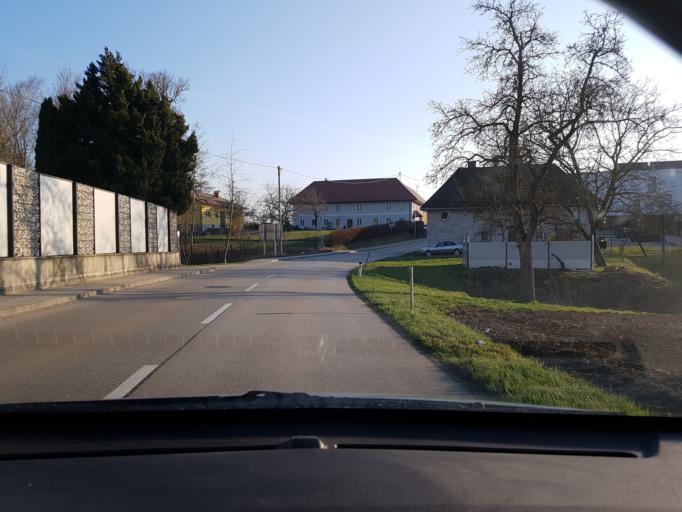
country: AT
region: Upper Austria
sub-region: Politischer Bezirk Linz-Land
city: Ansfelden
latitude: 48.1706
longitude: 14.2569
